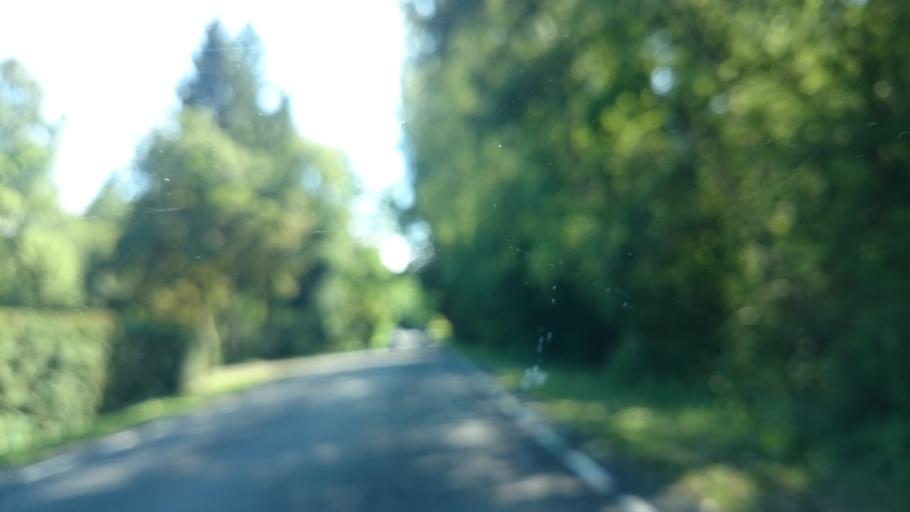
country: EE
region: Saare
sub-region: Kuressaare linn
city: Kuressaare
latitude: 58.5769
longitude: 22.6866
